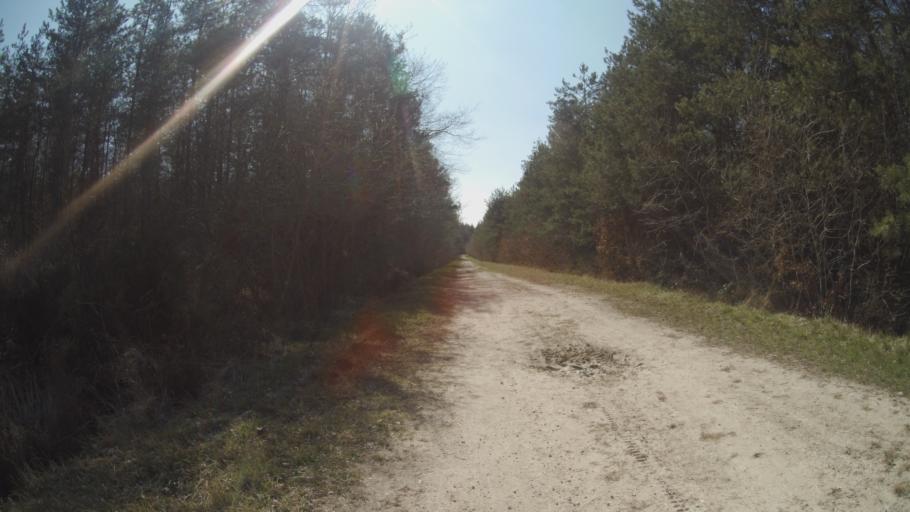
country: FR
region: Centre
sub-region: Departement du Loiret
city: Chanteau
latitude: 47.9525
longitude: 1.9634
